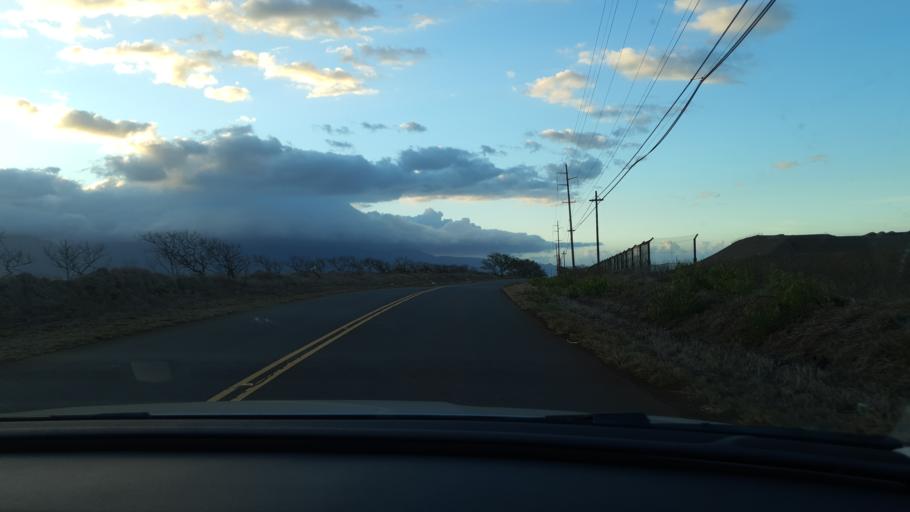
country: US
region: Hawaii
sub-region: Maui County
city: Kahului
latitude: 20.8540
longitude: -156.4206
